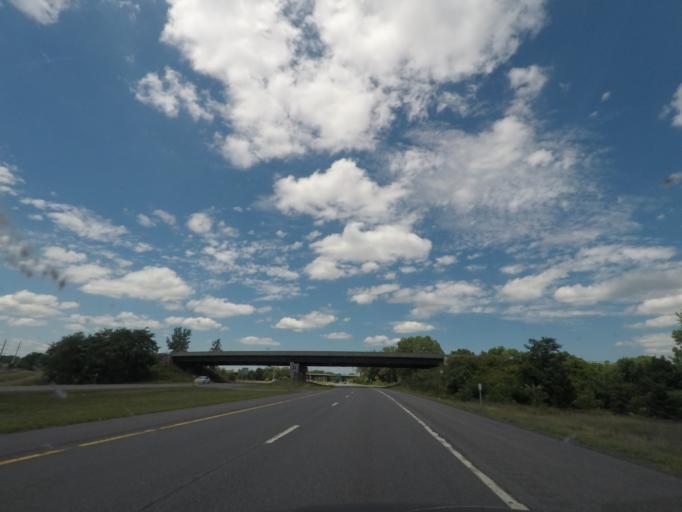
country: US
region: New York
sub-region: Albany County
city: McKownville
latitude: 42.6951
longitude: -73.8343
